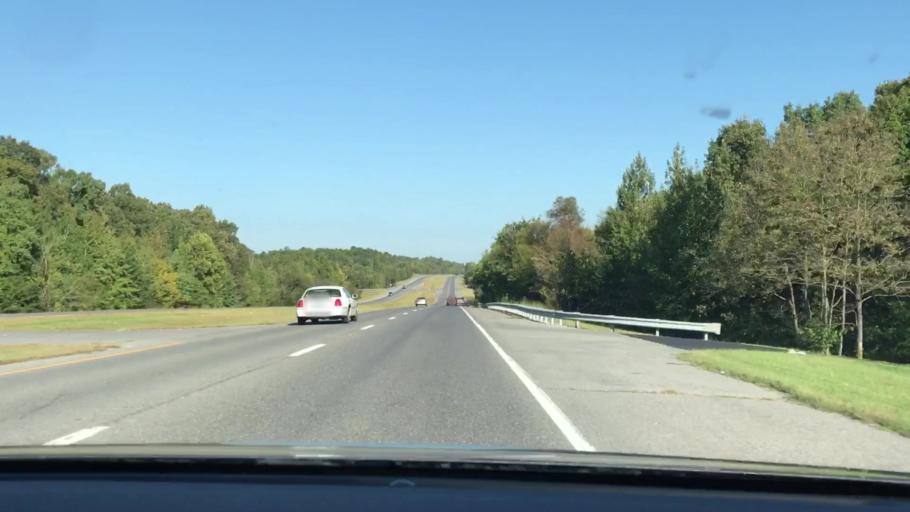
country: US
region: Kentucky
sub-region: Marshall County
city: Benton
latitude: 36.7715
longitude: -88.3157
